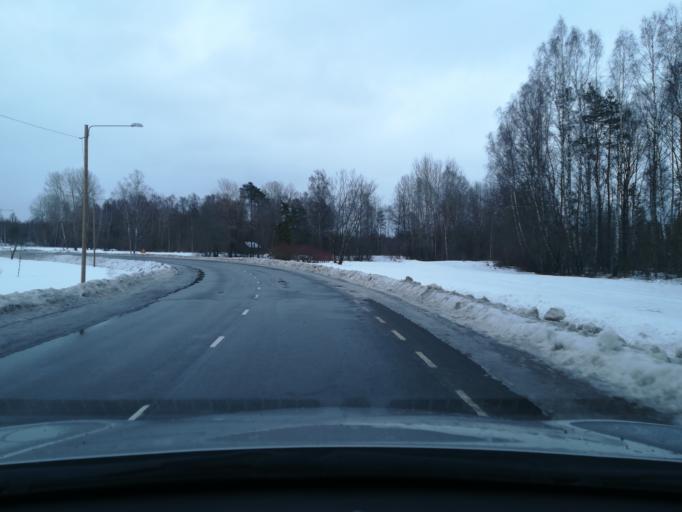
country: EE
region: Harju
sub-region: Nissi vald
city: Turba
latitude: 59.0743
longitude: 24.2412
